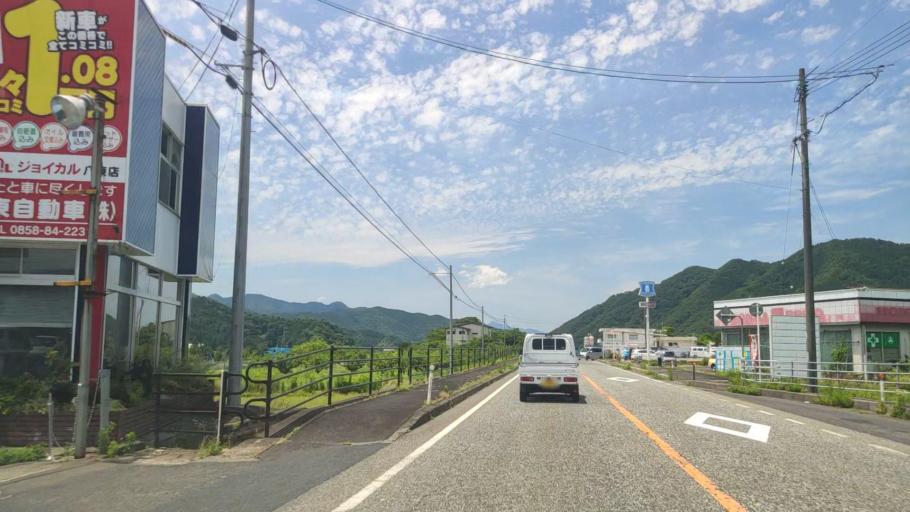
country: JP
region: Tottori
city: Tottori
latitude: 35.3627
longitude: 134.3480
